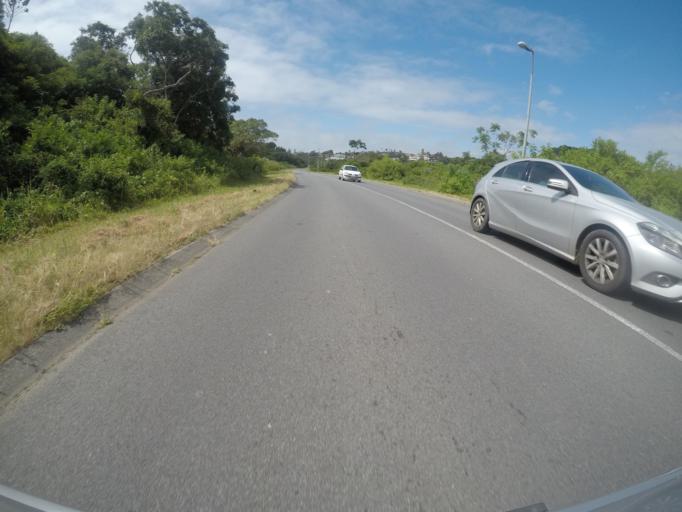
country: ZA
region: Eastern Cape
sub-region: Buffalo City Metropolitan Municipality
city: East London
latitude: -32.9775
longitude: 27.9333
